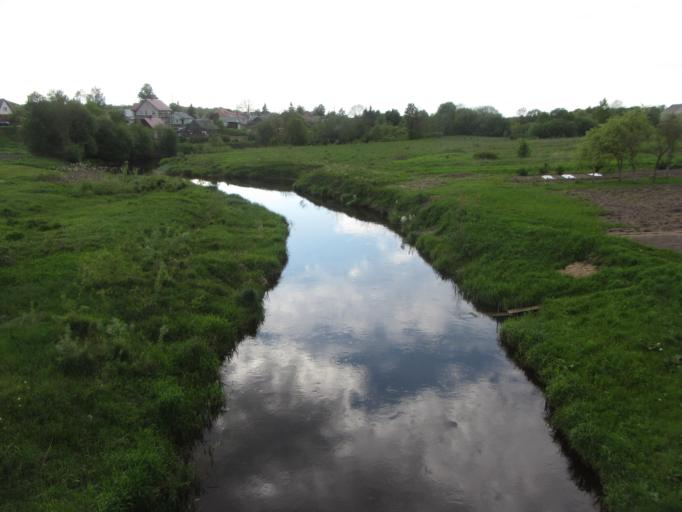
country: LT
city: Sirvintos
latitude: 55.0500
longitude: 24.9465
